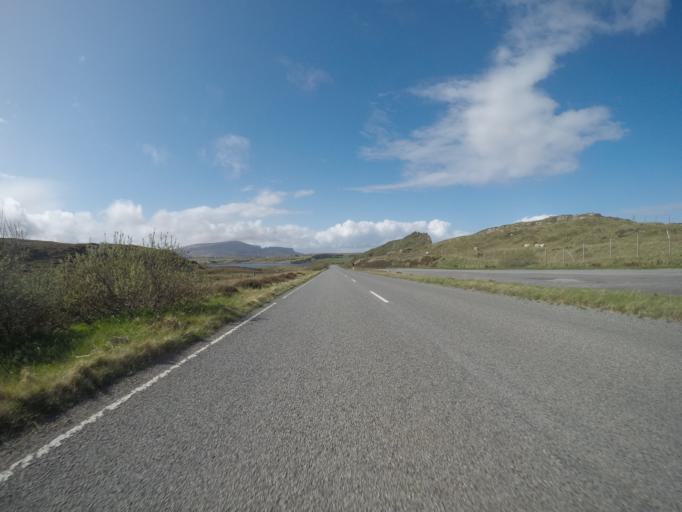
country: GB
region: Scotland
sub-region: Highland
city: Portree
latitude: 57.6021
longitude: -6.1670
